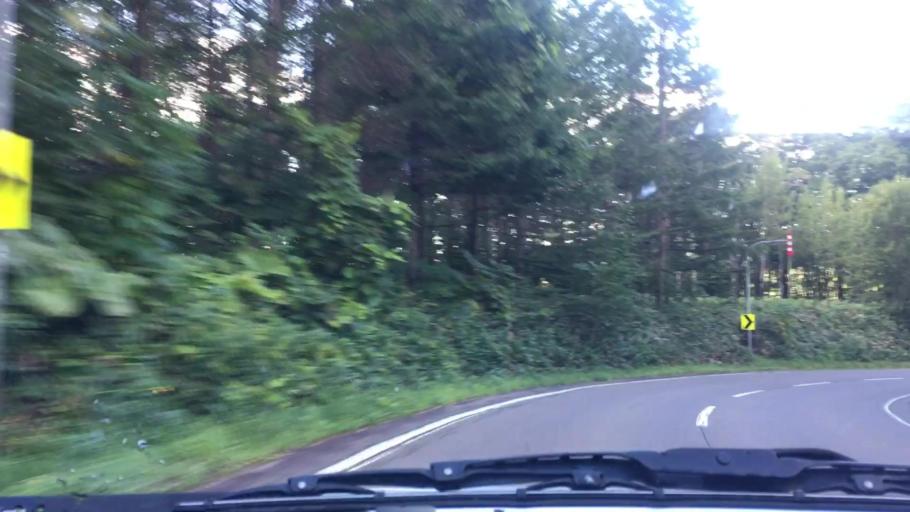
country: JP
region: Hokkaido
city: Otofuke
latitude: 43.1762
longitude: 142.9255
